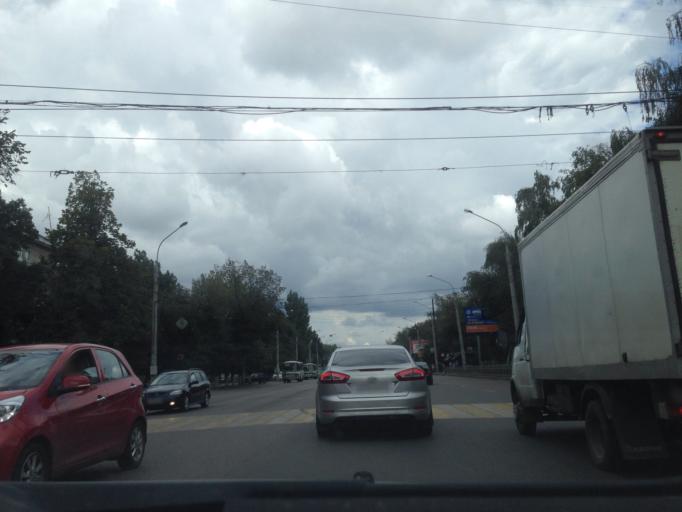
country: RU
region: Voronezj
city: Voronezh
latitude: 51.6791
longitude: 39.1849
